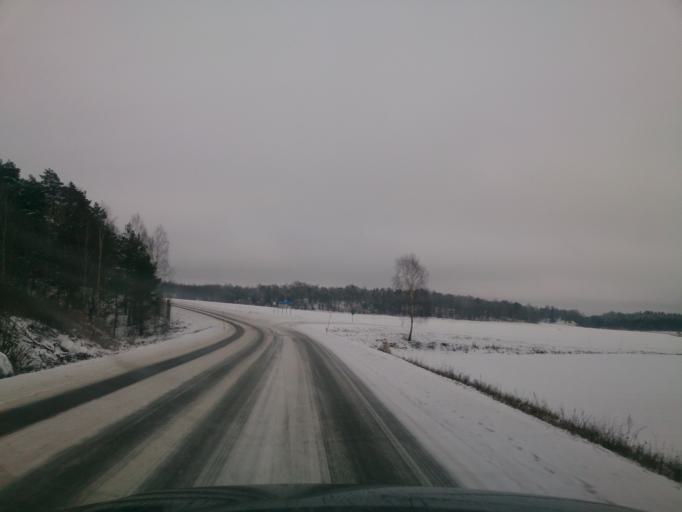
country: SE
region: OEstergoetland
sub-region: Norrkopings Kommun
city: Kimstad
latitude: 58.3983
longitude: 15.9522
